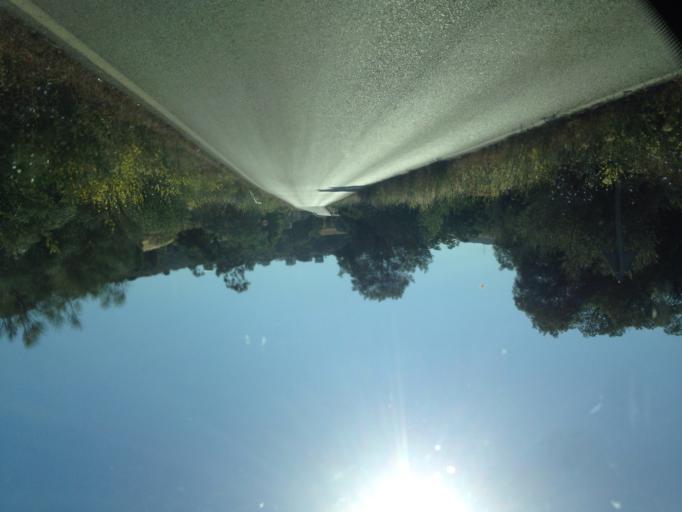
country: ES
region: Andalusia
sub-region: Provincia de Malaga
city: Casabermeja
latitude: 36.9011
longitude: -4.4544
